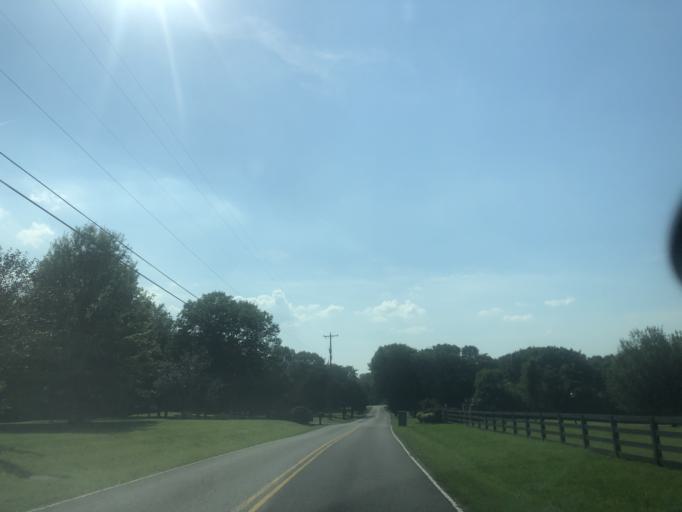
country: US
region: Tennessee
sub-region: Wilson County
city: Green Hill
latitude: 36.1452
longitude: -86.5920
